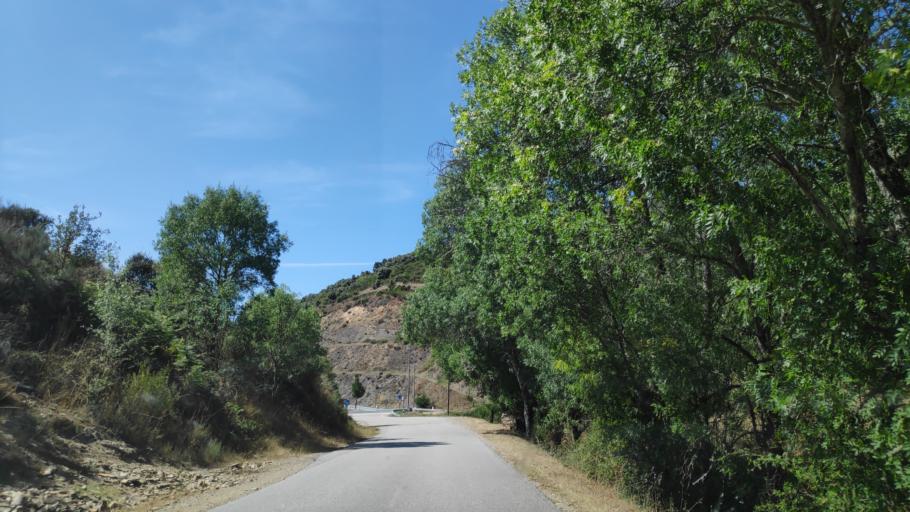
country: ES
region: Castille and Leon
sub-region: Provincia de Zamora
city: Trabazos
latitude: 41.7383
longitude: -6.5795
